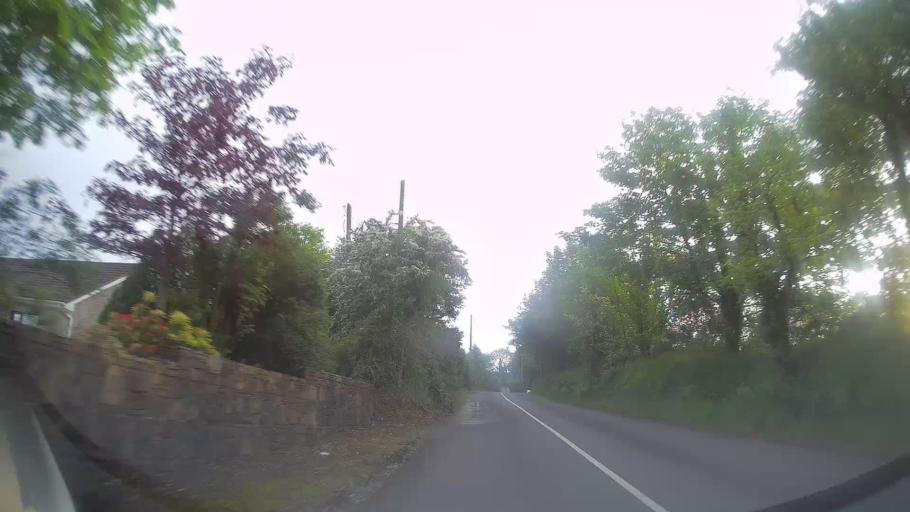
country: IE
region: Munster
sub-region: County Cork
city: Blarney
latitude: 51.9790
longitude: -8.5406
